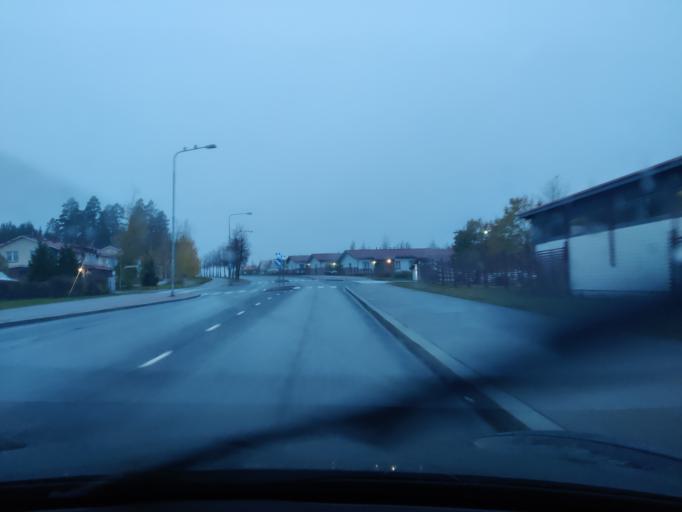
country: FI
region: Northern Savo
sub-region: Kuopio
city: Kuopio
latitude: 62.8265
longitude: 27.6876
